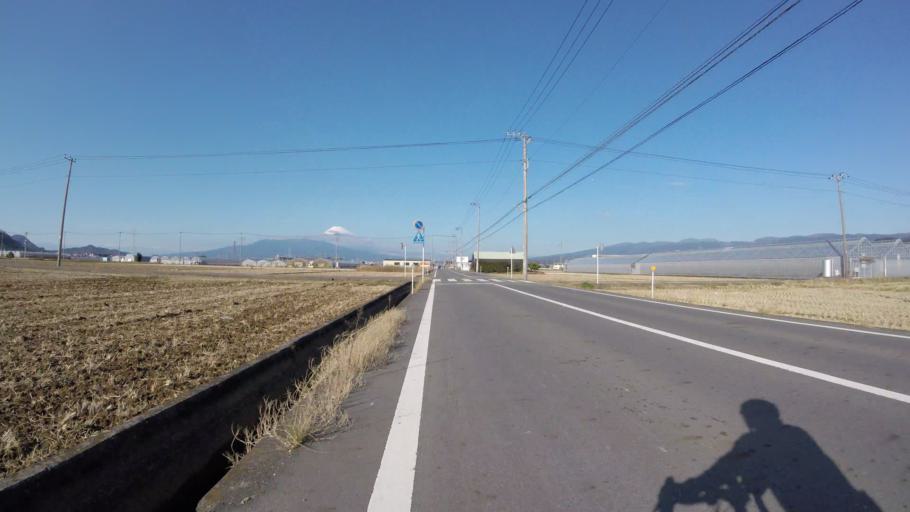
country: JP
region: Shizuoka
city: Mishima
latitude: 35.0617
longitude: 138.9526
